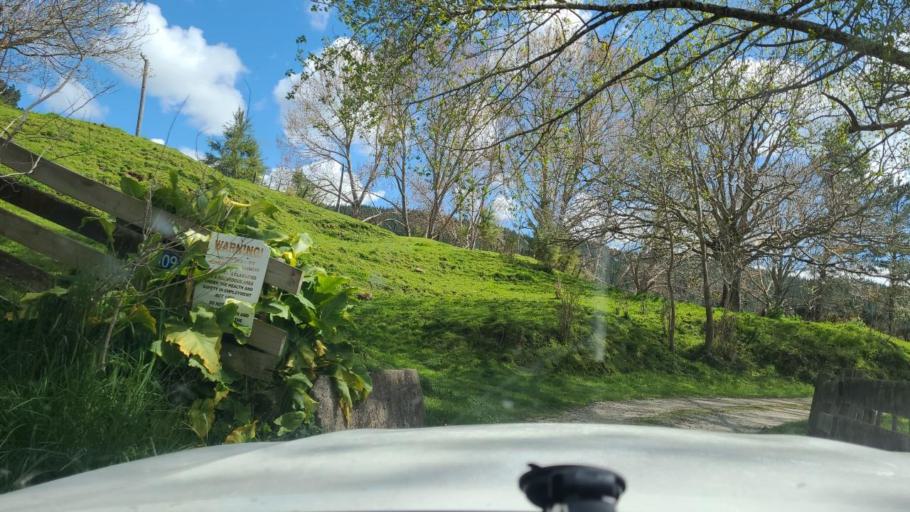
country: NZ
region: Gisborne
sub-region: Gisborne District
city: Gisborne
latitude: -38.7848
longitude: 177.7725
